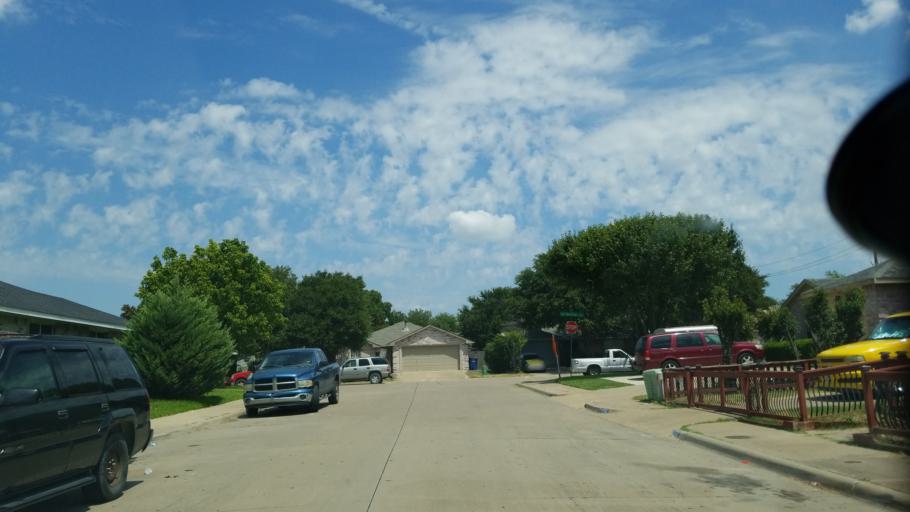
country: US
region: Texas
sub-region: Dallas County
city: Cockrell Hill
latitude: 32.7276
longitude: -96.8920
